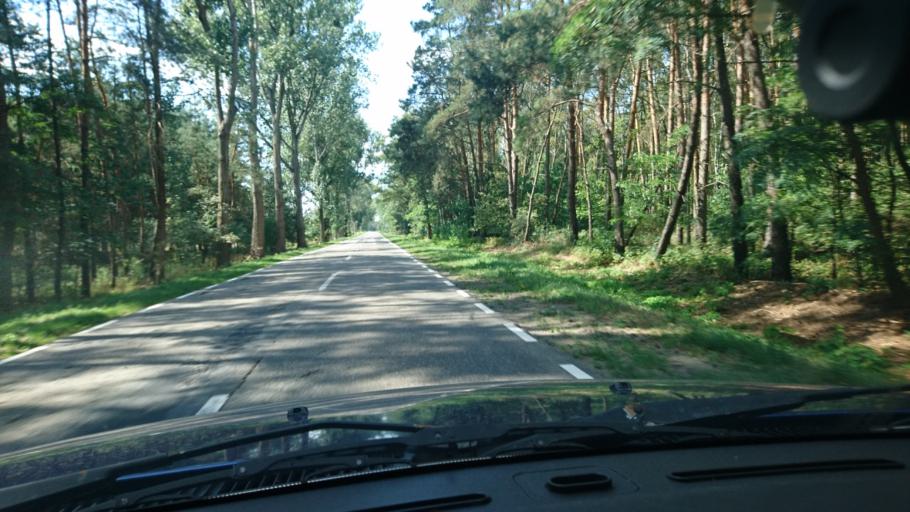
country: PL
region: Greater Poland Voivodeship
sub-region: Powiat ostrowski
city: Odolanow
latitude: 51.5922
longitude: 17.6308
